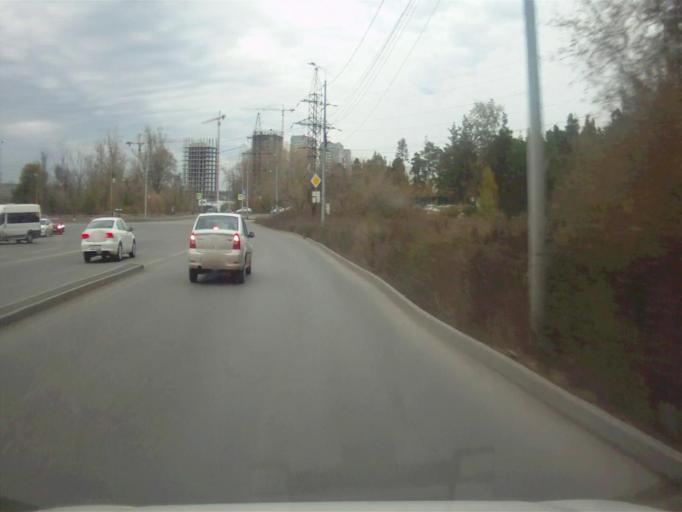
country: RU
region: Chelyabinsk
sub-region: Gorod Chelyabinsk
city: Chelyabinsk
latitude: 55.1691
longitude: 61.3571
